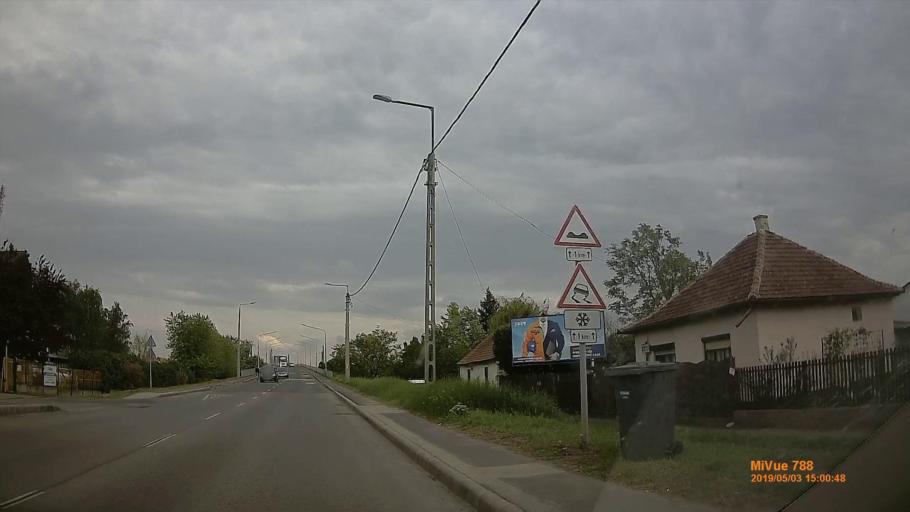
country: HU
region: Jasz-Nagykun-Szolnok
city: Szolnok
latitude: 47.1882
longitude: 20.1789
